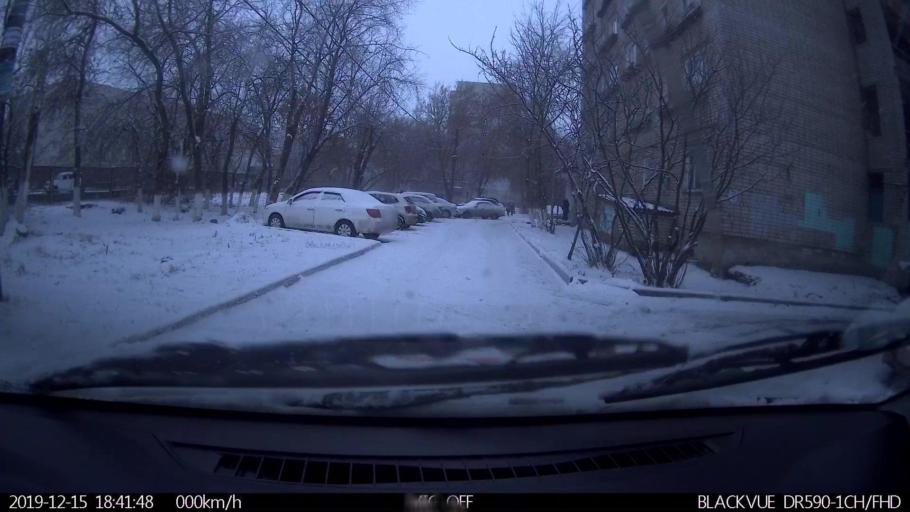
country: RU
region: Nizjnij Novgorod
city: Nizhniy Novgorod
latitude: 56.3268
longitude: 43.9222
